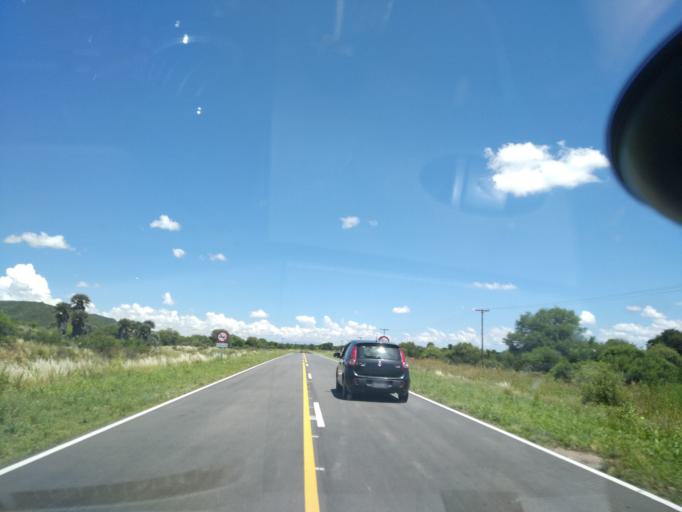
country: AR
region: Cordoba
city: Salsacate
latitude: -31.3772
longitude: -65.1012
